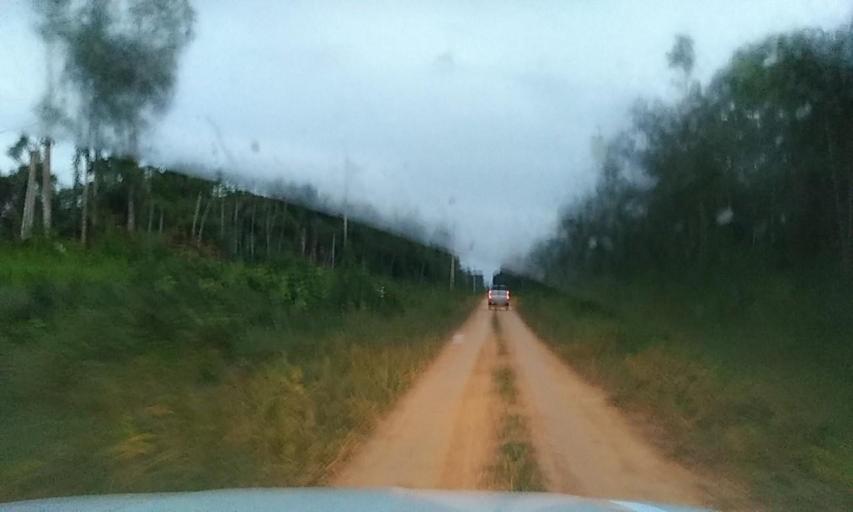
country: BR
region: Para
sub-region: Senador Jose Porfirio
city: Senador Jose Porfirio
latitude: -2.8990
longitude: -51.6851
